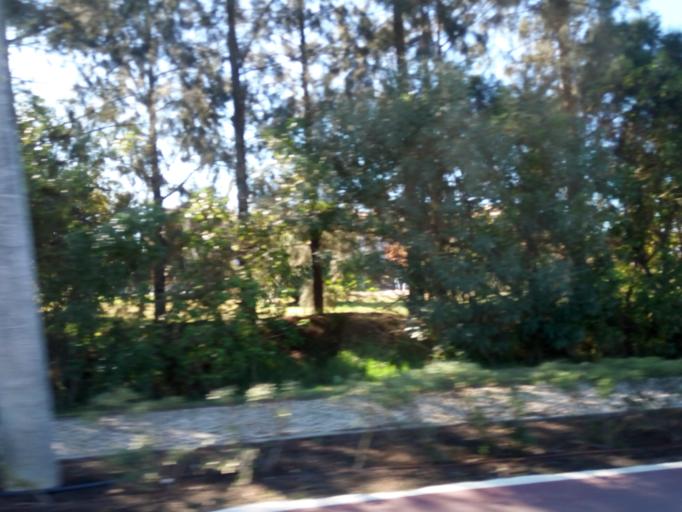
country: PT
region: Faro
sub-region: Loule
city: Vilamoura
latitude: 37.0895
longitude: -8.1228
